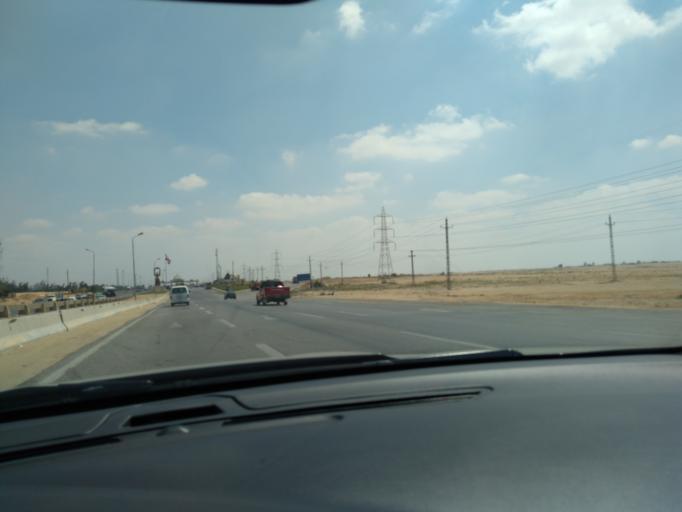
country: EG
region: Al Isma'iliyah
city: At Tall al Kabir
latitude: 30.4038
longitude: 31.9924
